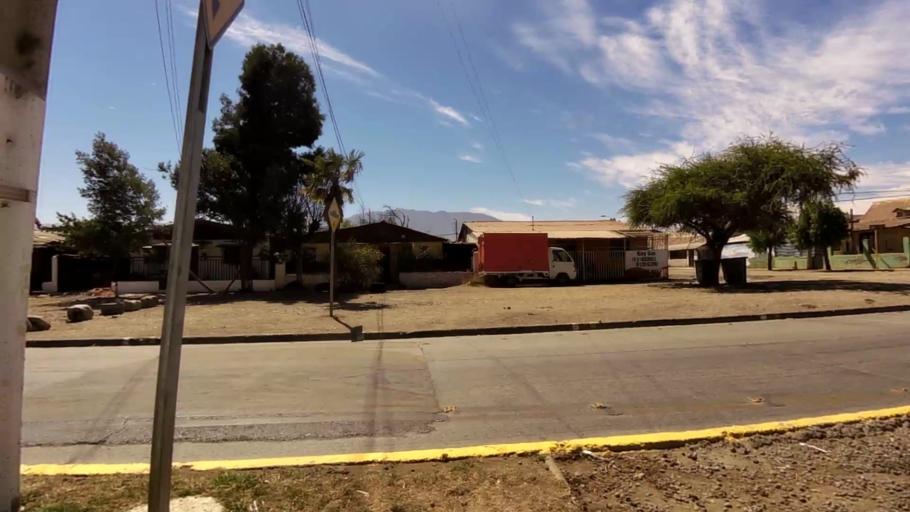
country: CL
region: O'Higgins
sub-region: Provincia de Cachapoal
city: Graneros
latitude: -33.9730
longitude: -70.7118
